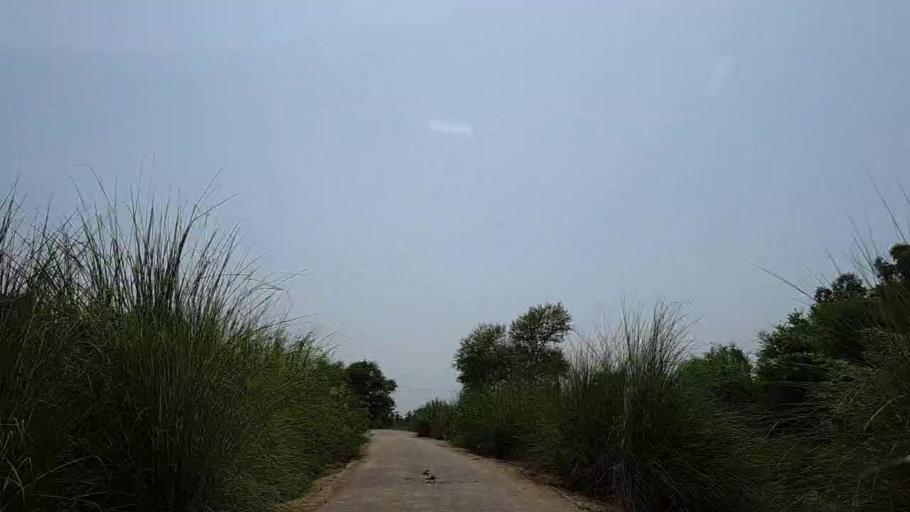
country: PK
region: Sindh
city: Adilpur
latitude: 27.9120
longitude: 69.3669
